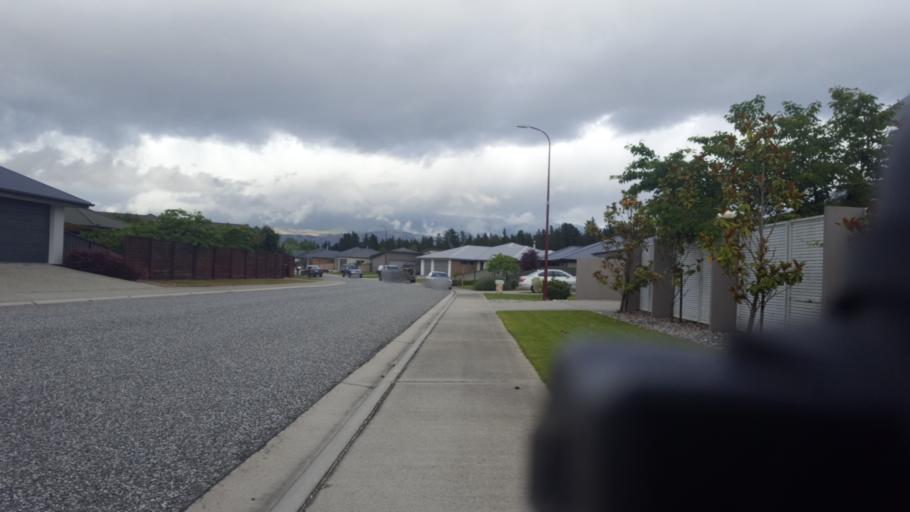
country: NZ
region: Otago
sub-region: Queenstown-Lakes District
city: Wanaka
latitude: -45.2384
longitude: 169.3805
